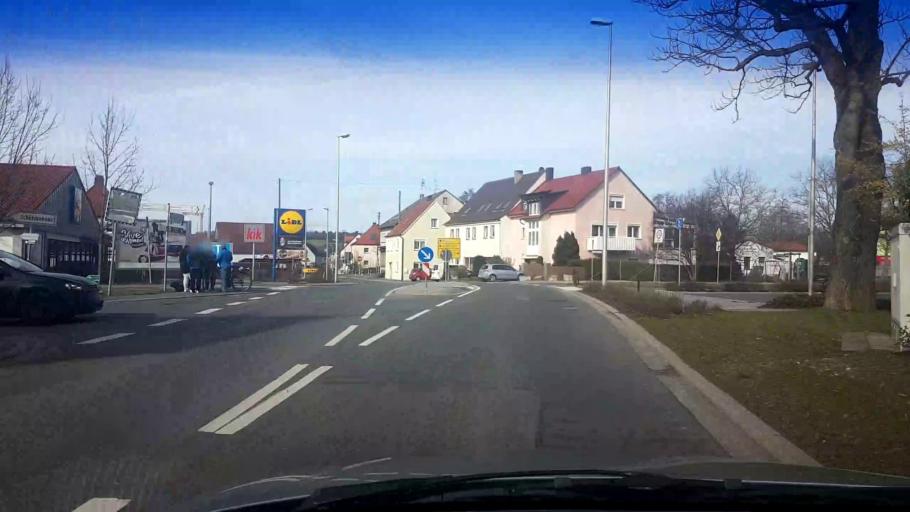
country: DE
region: Bavaria
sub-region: Upper Franconia
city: Burgebrach
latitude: 49.8257
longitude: 10.7380
